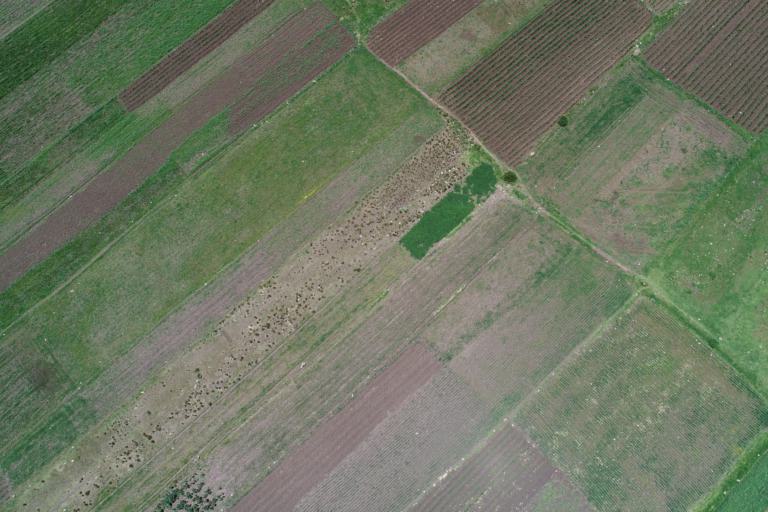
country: BO
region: La Paz
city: Achacachi
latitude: -16.0197
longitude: -68.7901
